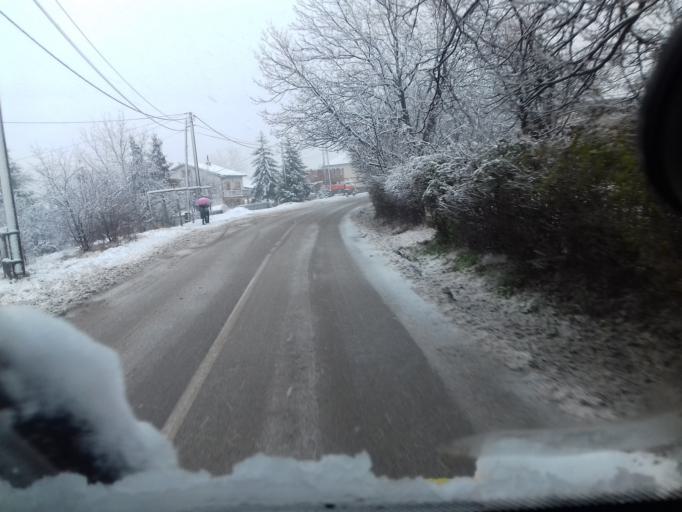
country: BA
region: Federation of Bosnia and Herzegovina
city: Zenica
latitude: 44.1873
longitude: 17.9437
